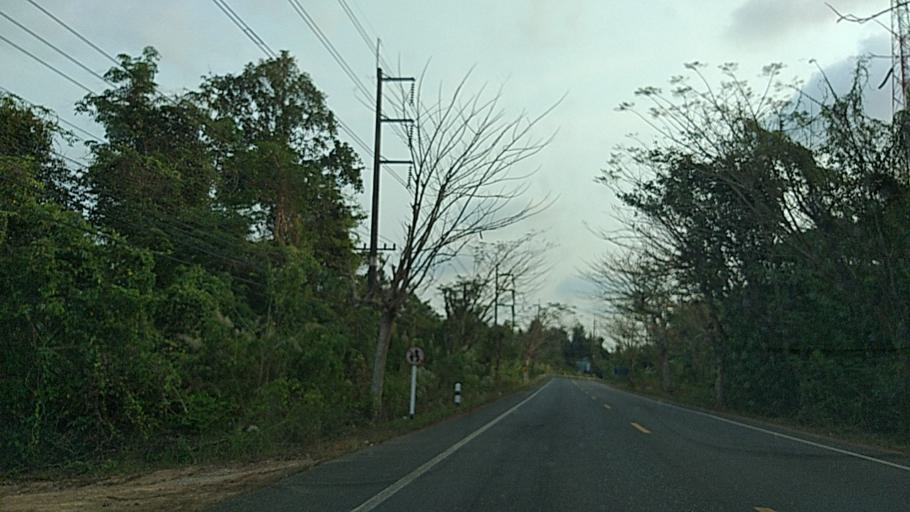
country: TH
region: Trat
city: Laem Ngop
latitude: 12.2679
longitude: 102.3057
